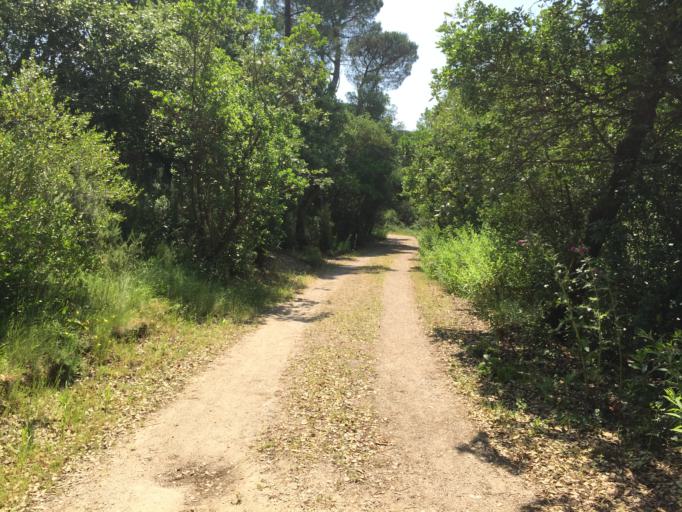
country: PT
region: Lisbon
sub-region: Mafra
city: Milharado
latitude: 38.9027
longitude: -9.1818
